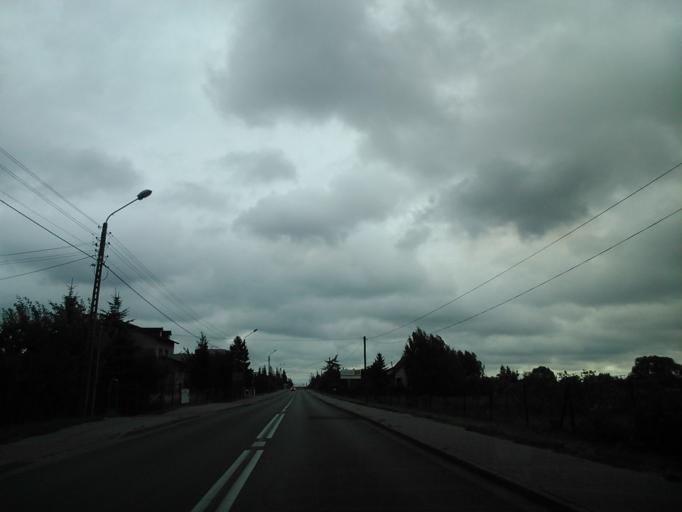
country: PL
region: Kujawsko-Pomorskie
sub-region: Powiat inowroclawski
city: Inowroclaw
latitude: 52.7955
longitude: 18.2815
